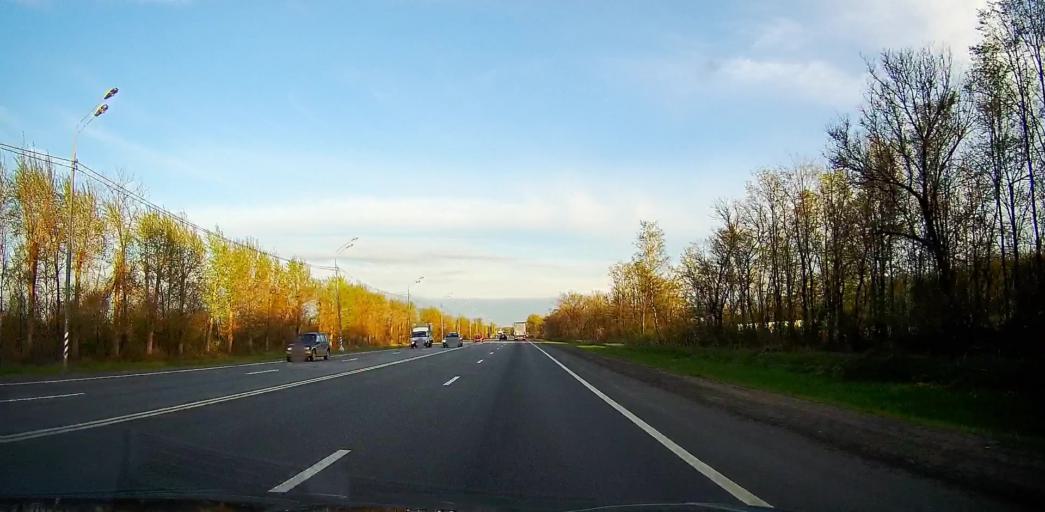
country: RU
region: Moskovskaya
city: Troitskoye
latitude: 55.2676
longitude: 38.5026
